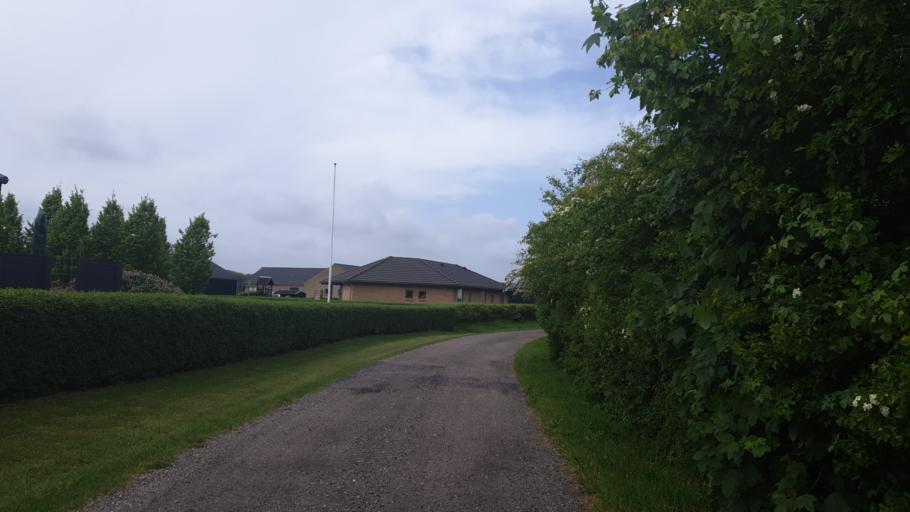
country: DK
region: Central Jutland
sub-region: Hedensted Kommune
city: Hedensted
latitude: 55.8136
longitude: 9.6989
